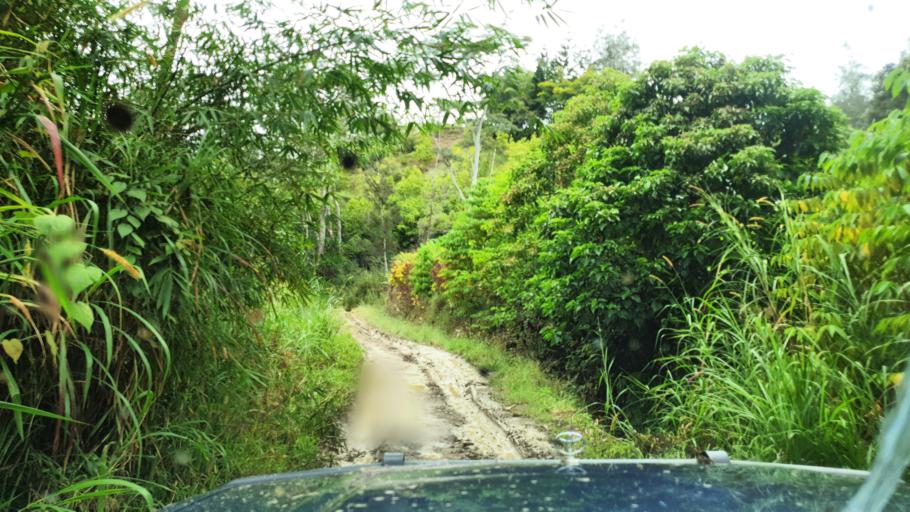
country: PG
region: Jiwaka
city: Minj
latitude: -5.9269
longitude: 144.7420
